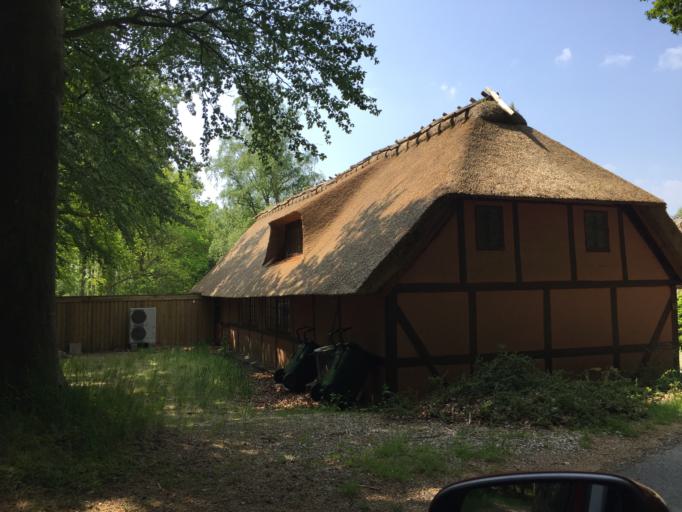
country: DK
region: South Denmark
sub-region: Langeland Kommune
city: Rudkobing
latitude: 54.9899
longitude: 10.8243
